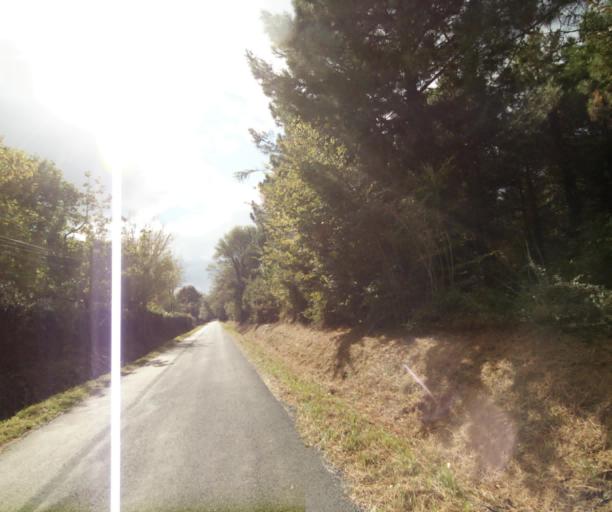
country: FR
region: Languedoc-Roussillon
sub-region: Departement des Pyrenees-Orientales
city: Argelers
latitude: 42.5668
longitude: 3.0283
